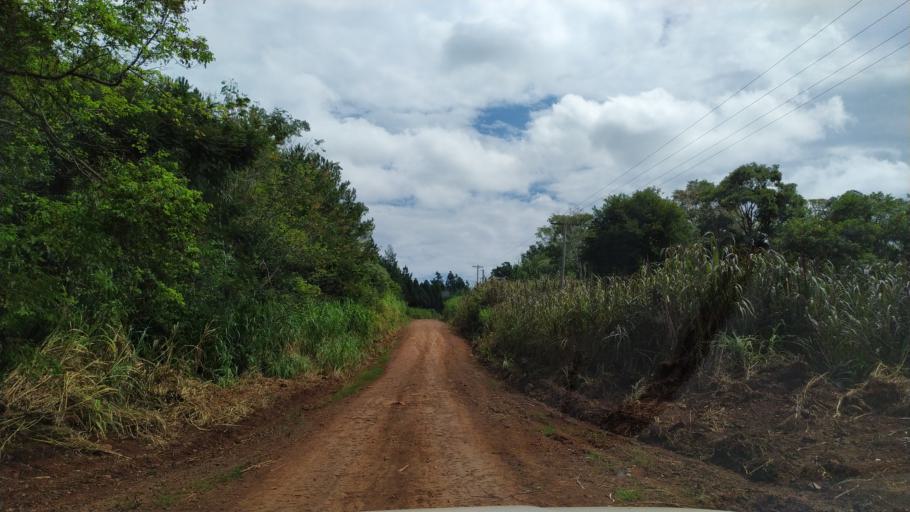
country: AR
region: Misiones
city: Puerto Piray
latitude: -26.5360
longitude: -54.6430
